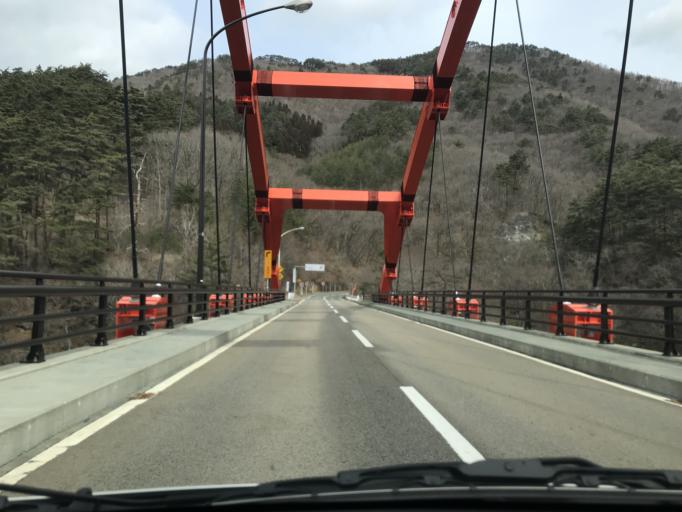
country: JP
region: Iwate
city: Tono
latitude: 39.3030
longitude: 141.3452
